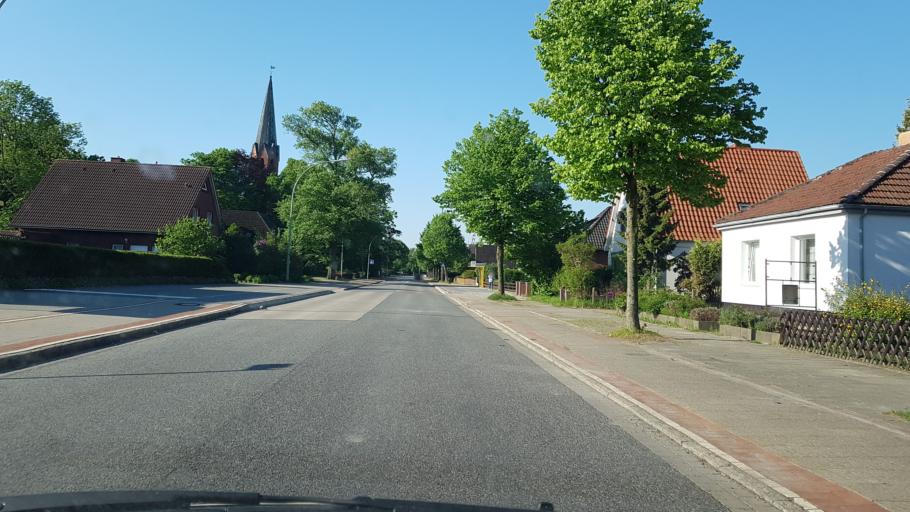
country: DE
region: Lower Saxony
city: Wremen
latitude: 53.6067
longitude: 8.5353
